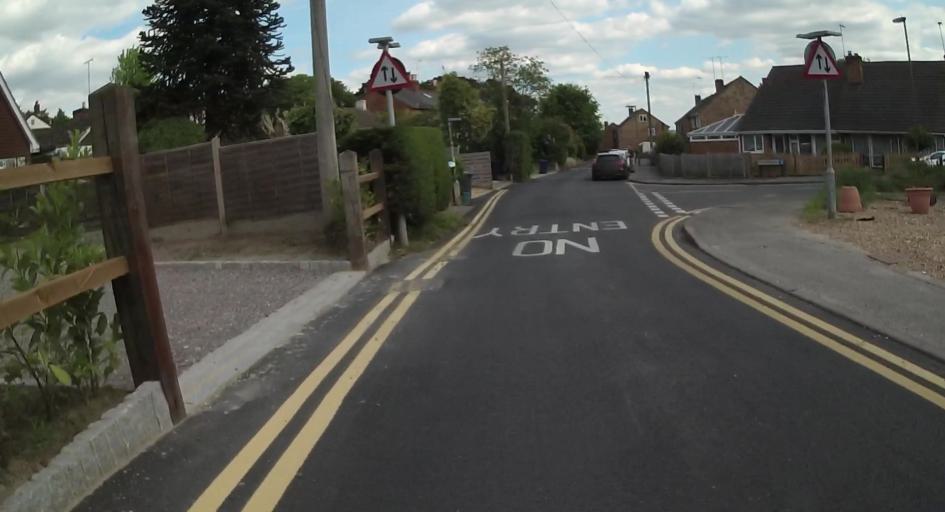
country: GB
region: England
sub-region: Surrey
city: Hale
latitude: 51.2378
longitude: -0.7863
